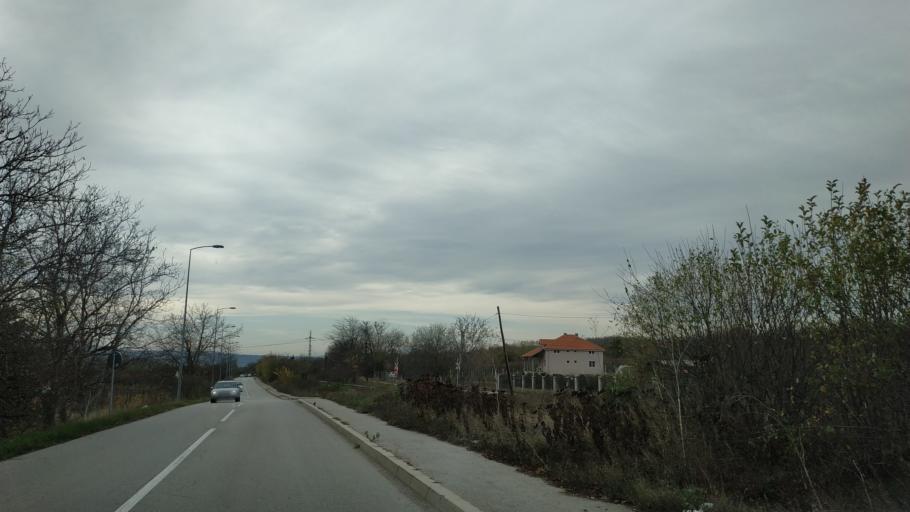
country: RS
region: Central Serbia
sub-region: Nisavski Okrug
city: Nis
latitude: 43.3495
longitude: 21.9390
